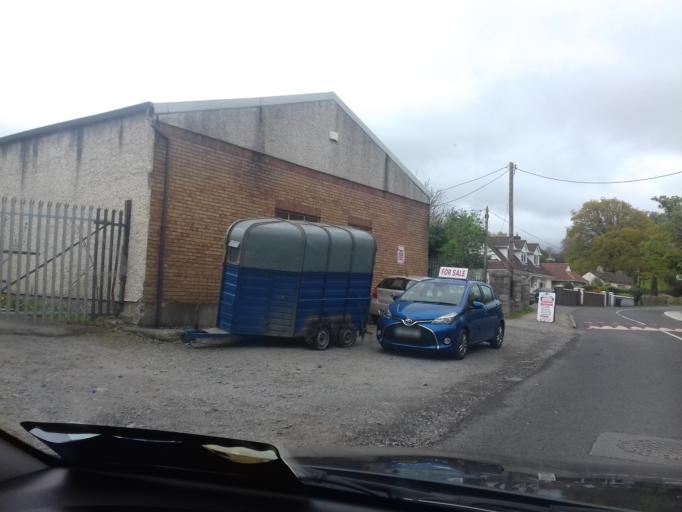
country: IE
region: Leinster
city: Ballyboden
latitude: 53.2769
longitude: -6.2971
